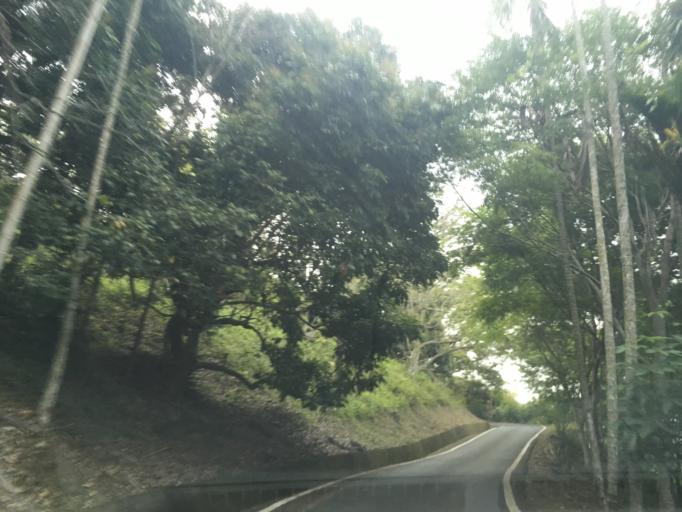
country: TW
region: Taiwan
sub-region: Nantou
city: Puli
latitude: 23.9464
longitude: 120.8478
